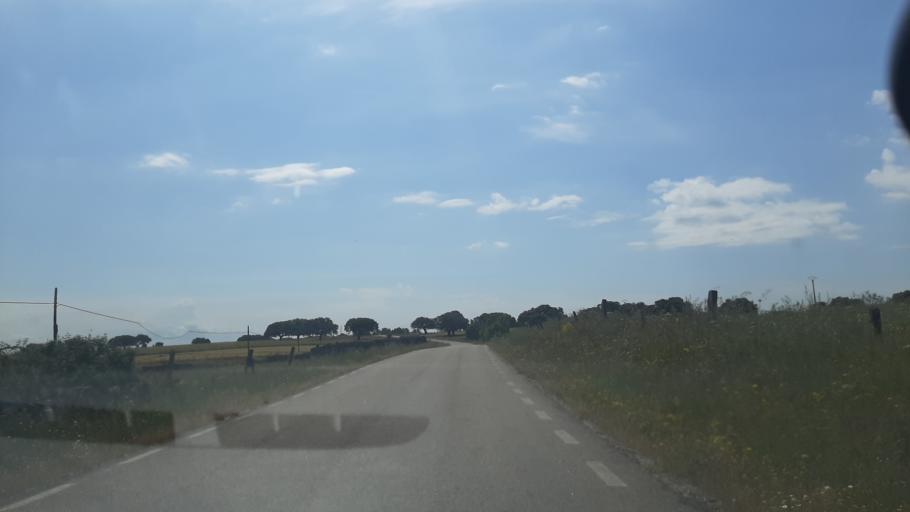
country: ES
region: Castille and Leon
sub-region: Provincia de Salamanca
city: Gallegos de Arganan
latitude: 40.6454
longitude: -6.7466
